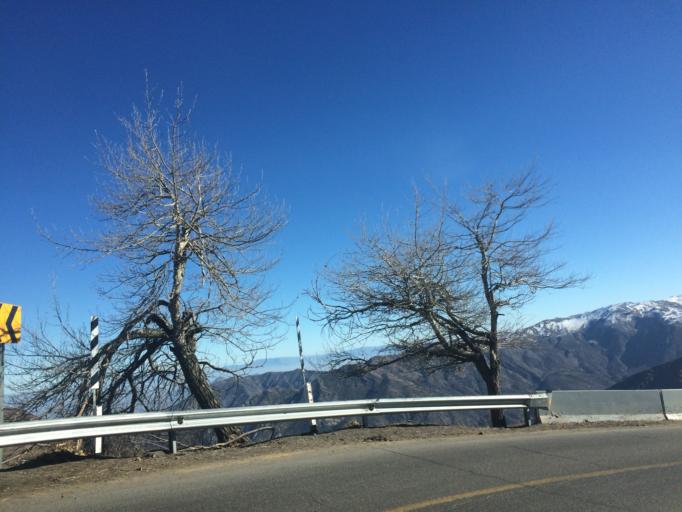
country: CL
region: Santiago Metropolitan
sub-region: Provincia de Santiago
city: Villa Presidente Frei, Nunoa, Santiago, Chile
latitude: -33.3559
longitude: -70.3185
